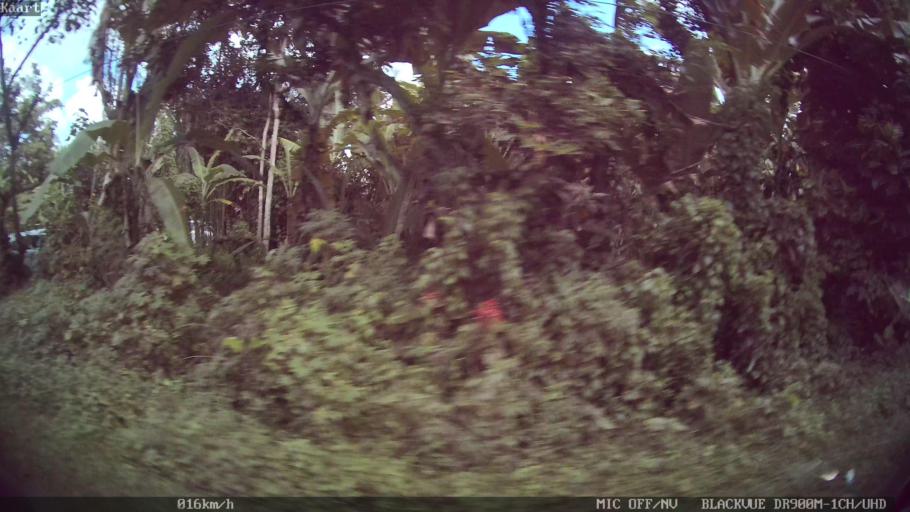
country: ID
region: Bali
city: Banjar Tebongkang
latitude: -8.5392
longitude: 115.2518
